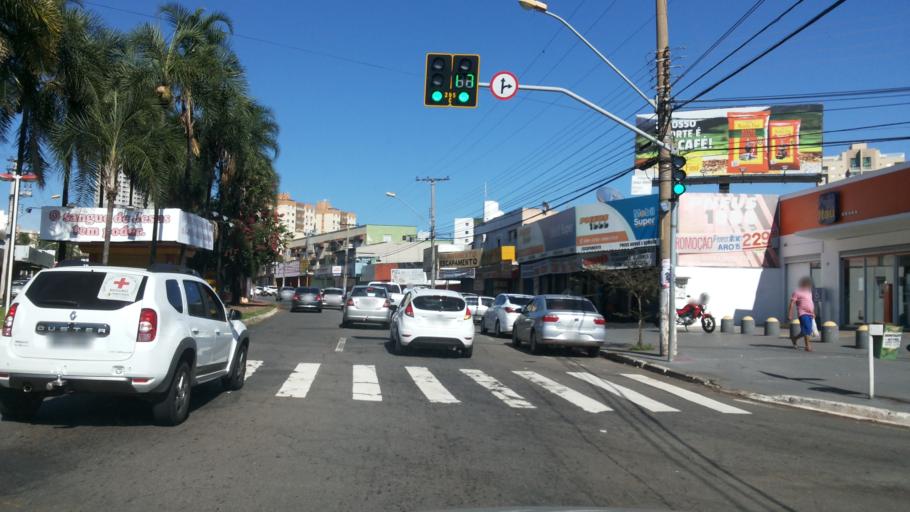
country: BR
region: Goias
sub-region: Goiania
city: Goiania
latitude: -16.7120
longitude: -49.2536
